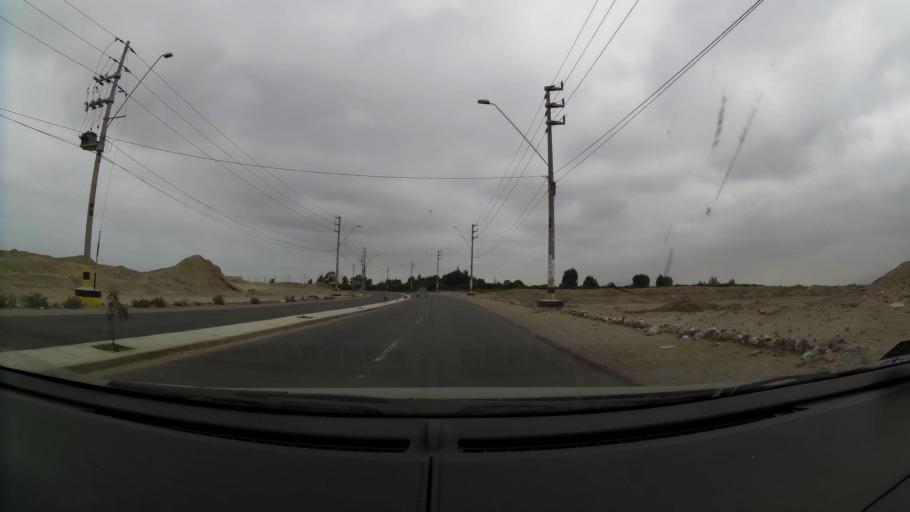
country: PE
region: La Libertad
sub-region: Provincia de Trujillo
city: La Esperanza
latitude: -8.0953
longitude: -79.0712
